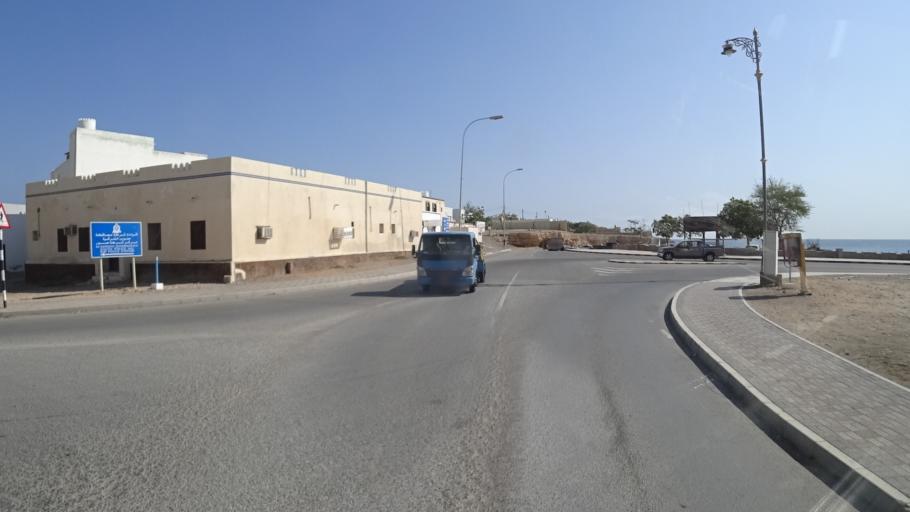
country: OM
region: Ash Sharqiyah
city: Sur
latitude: 22.5728
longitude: 59.5273
